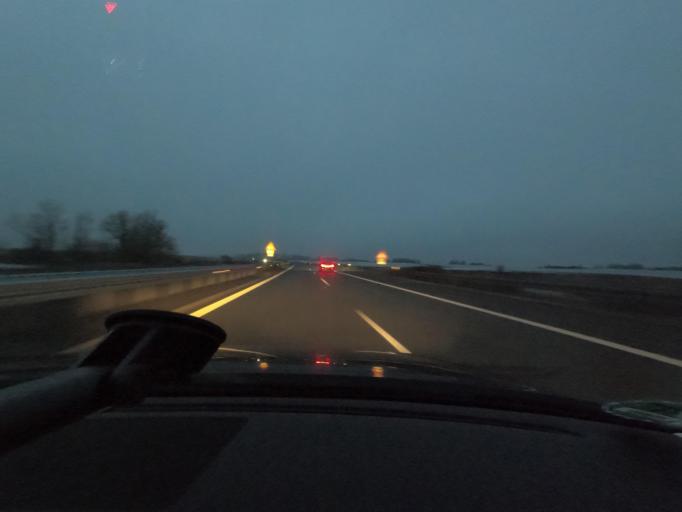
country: DE
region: Bavaria
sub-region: Upper Franconia
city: Meeder
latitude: 50.3333
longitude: 10.9377
